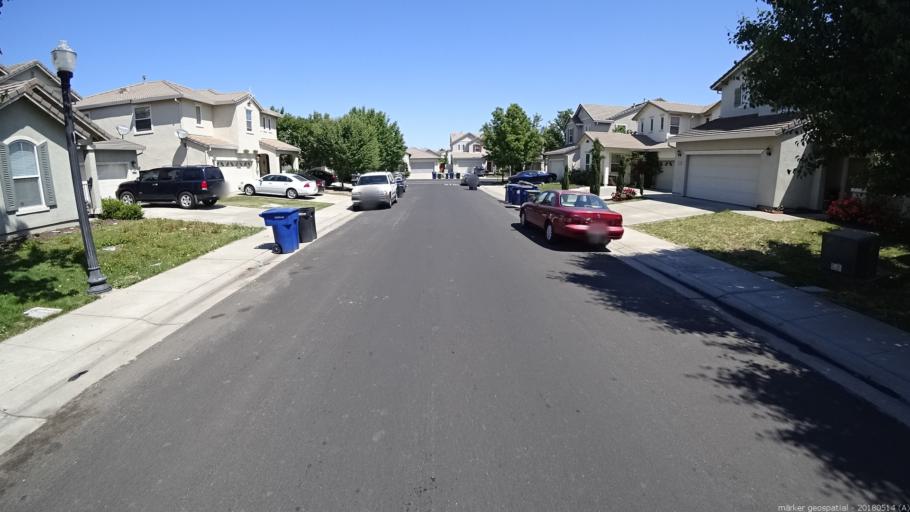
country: US
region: California
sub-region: Yolo County
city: West Sacramento
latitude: 38.6303
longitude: -121.5252
